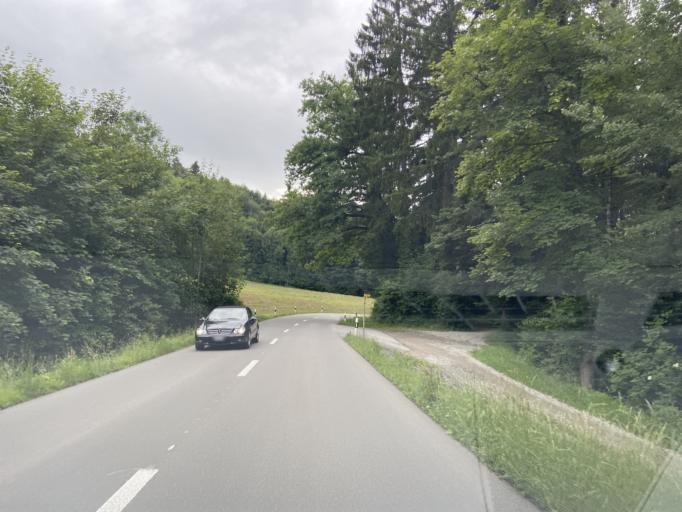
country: CH
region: Thurgau
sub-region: Muenchwilen District
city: Aadorf
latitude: 47.4655
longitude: 8.8930
